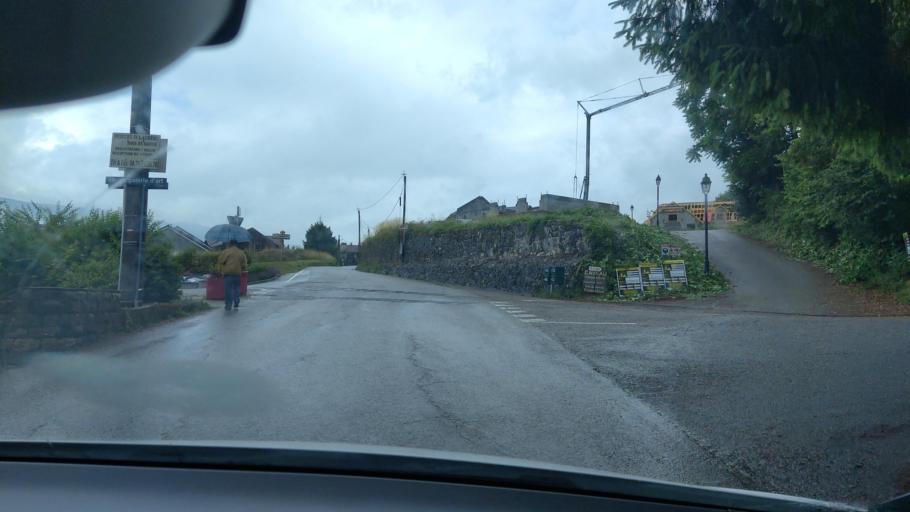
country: FR
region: Rhone-Alpes
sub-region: Departement de la Savoie
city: Chindrieux
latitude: 45.8219
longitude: 5.8516
